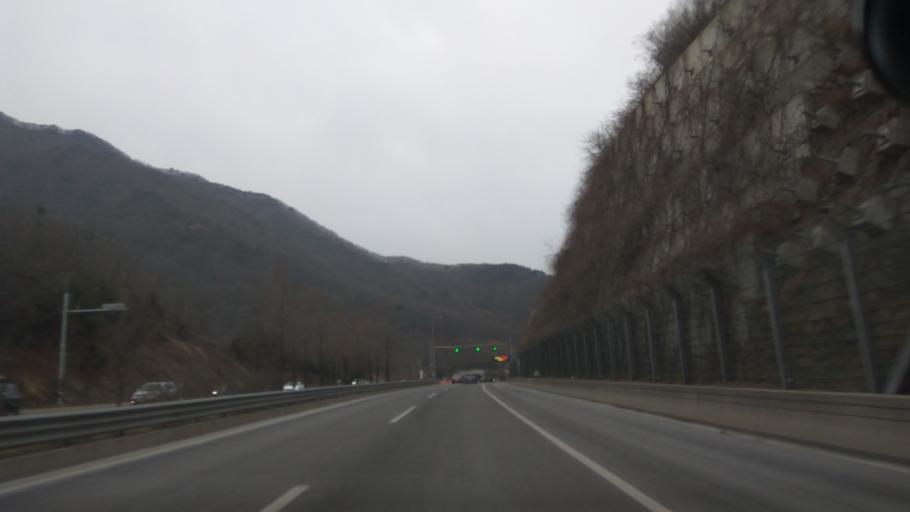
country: KR
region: Gyeonggi-do
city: Cheongpyeong
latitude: 37.6496
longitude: 127.4565
